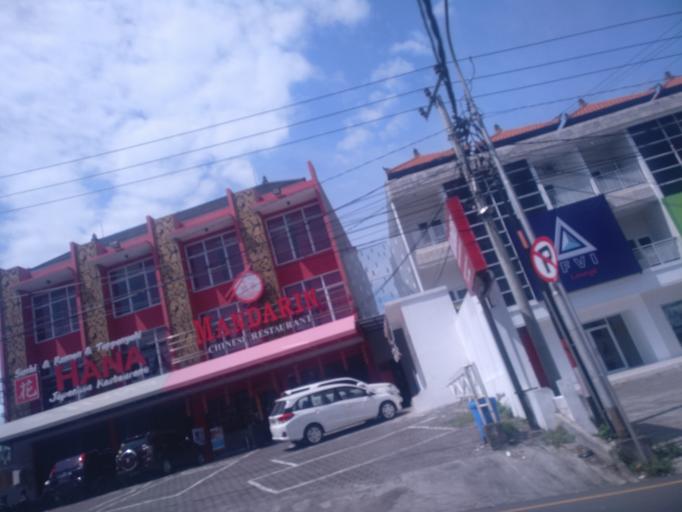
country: ID
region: Bali
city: Banjar Kertasari
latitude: -8.6362
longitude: 115.1928
